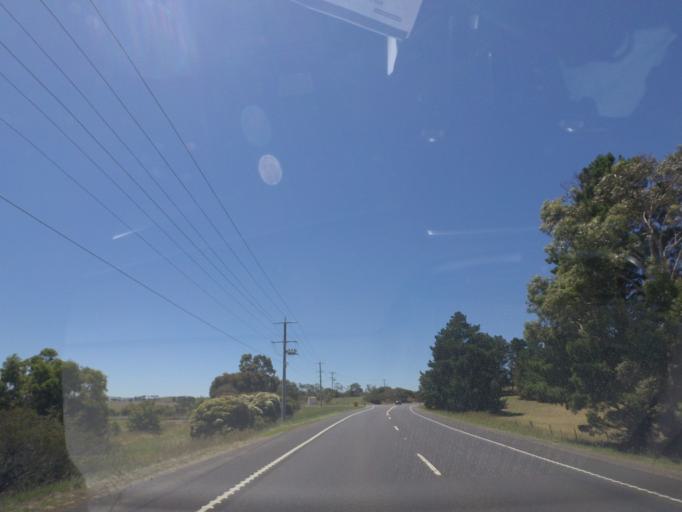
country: AU
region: Victoria
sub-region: Whittlesea
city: Whittlesea
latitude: -37.4756
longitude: 145.0246
